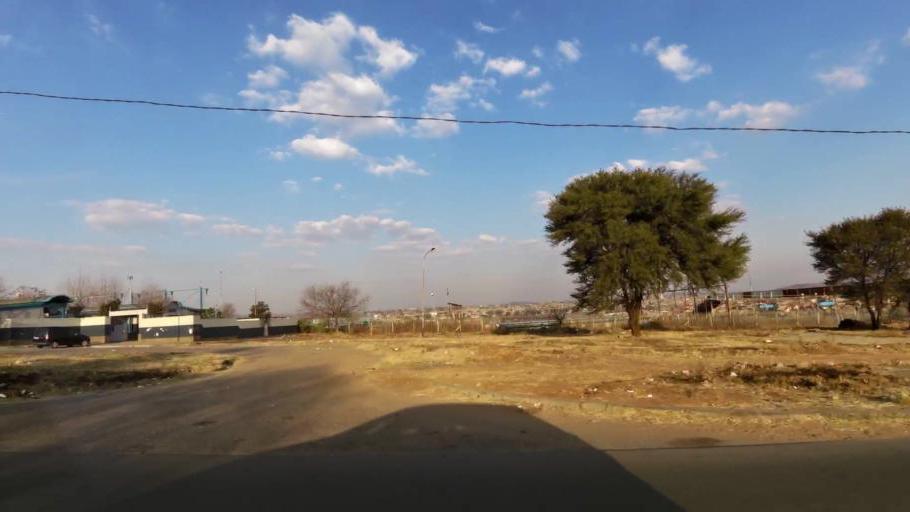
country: ZA
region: Gauteng
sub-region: City of Johannesburg Metropolitan Municipality
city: Soweto
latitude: -26.2267
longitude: 27.9076
